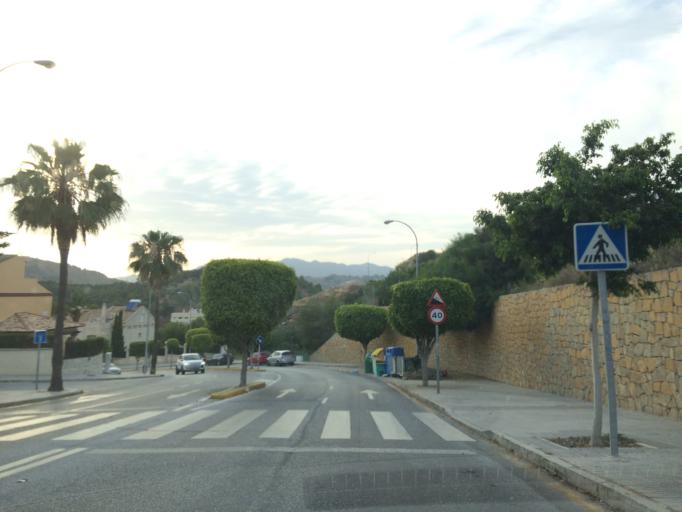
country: ES
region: Andalusia
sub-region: Provincia de Malaga
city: Malaga
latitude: 36.7273
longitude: -4.3865
